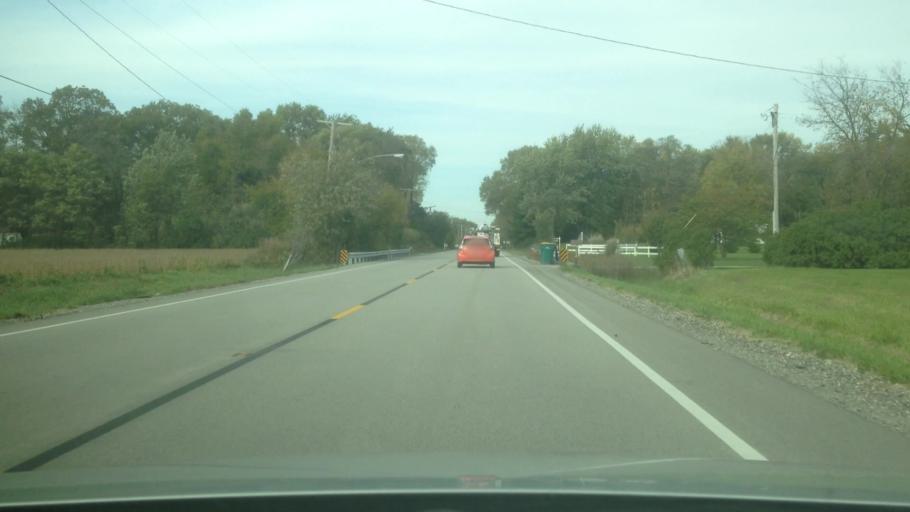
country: US
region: Illinois
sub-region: Will County
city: Wilmington
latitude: 41.2954
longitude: -88.1585
